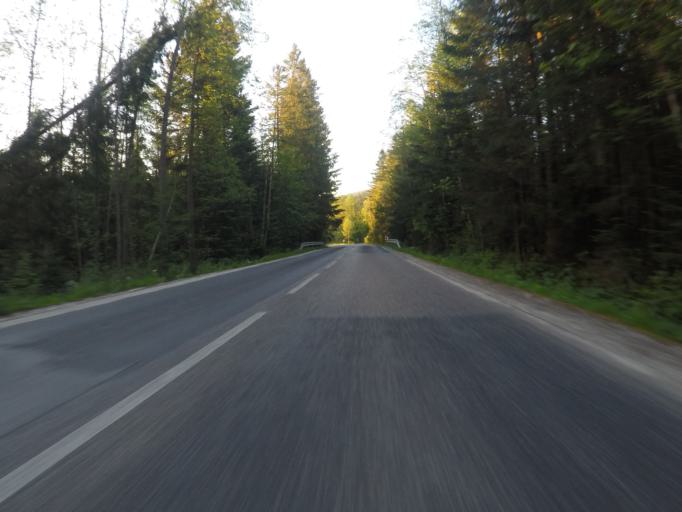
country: PL
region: Lesser Poland Voivodeship
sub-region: Powiat tatrzanski
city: Bukowina Tatrzanska
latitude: 49.2867
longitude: 20.0854
